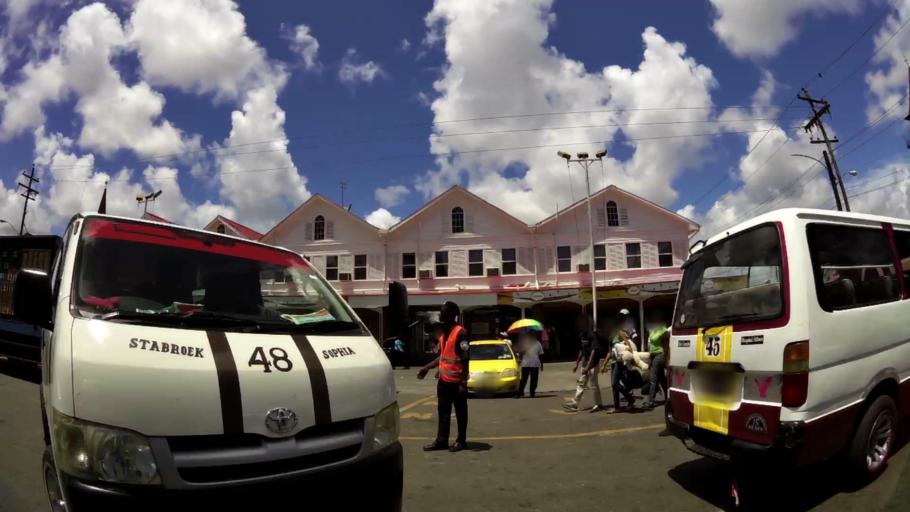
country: GY
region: Demerara-Mahaica
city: Georgetown
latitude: 6.8099
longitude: -58.1667
